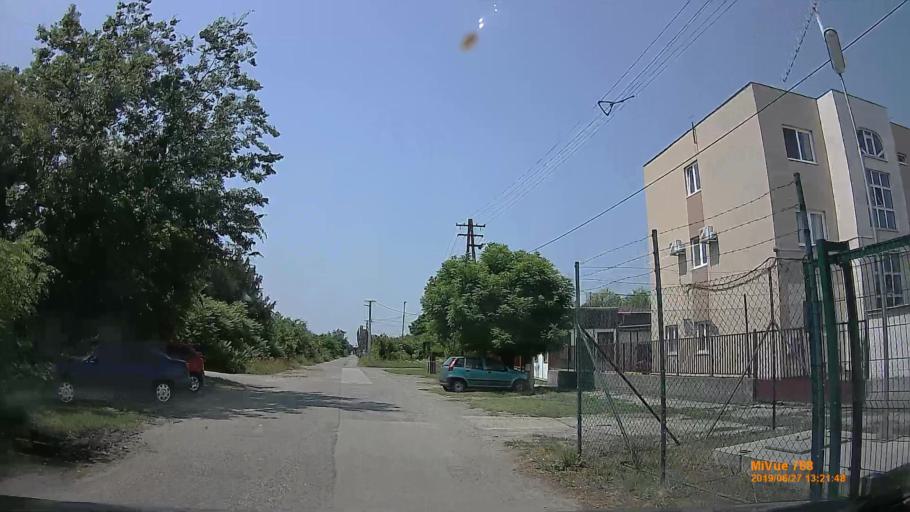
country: HU
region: Pest
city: Cegled
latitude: 47.1832
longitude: 19.8113
